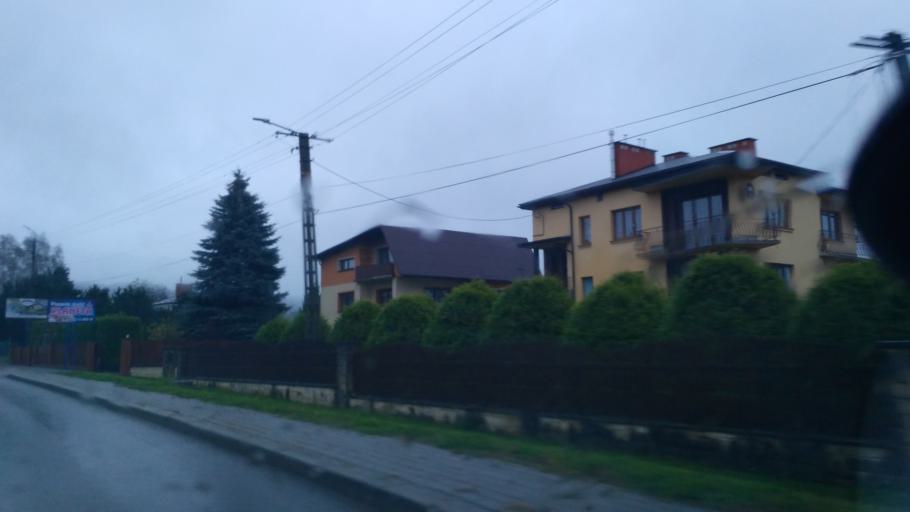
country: PL
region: Subcarpathian Voivodeship
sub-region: Powiat krosnienski
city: Korczyna
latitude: 49.7187
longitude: 21.8115
